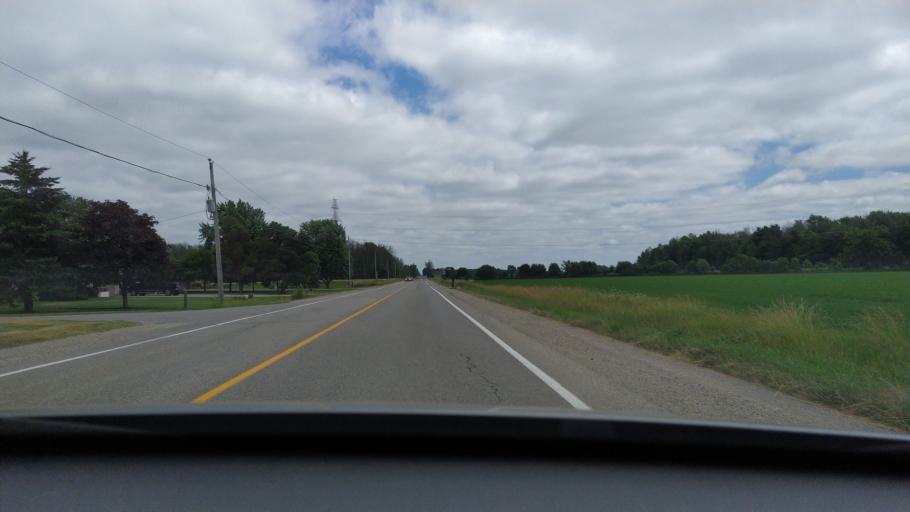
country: CA
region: Ontario
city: Stratford
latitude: 43.3464
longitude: -80.9686
